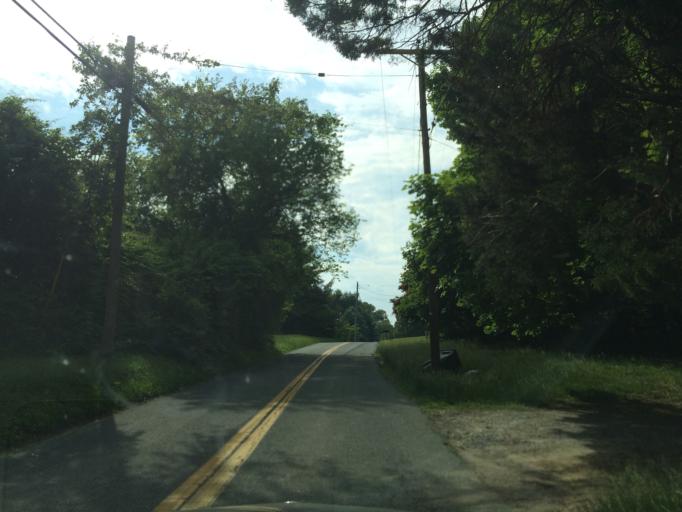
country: US
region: Maryland
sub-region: Baltimore County
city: Reisterstown
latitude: 39.4294
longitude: -76.8593
